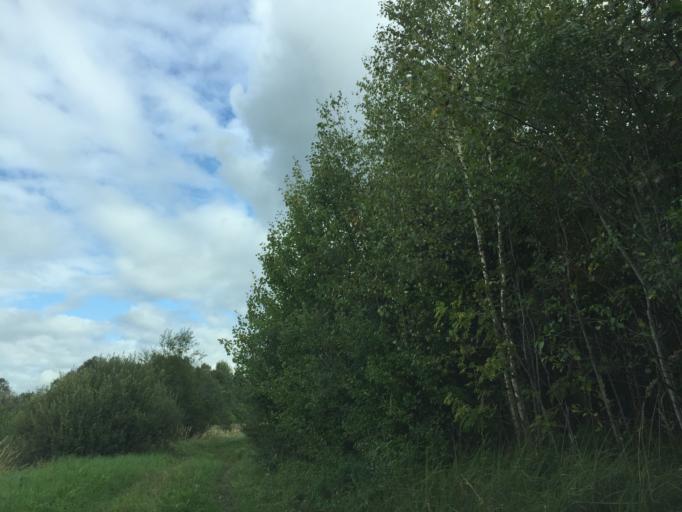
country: LV
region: Pargaujas
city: Stalbe
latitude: 57.4886
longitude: 24.9101
